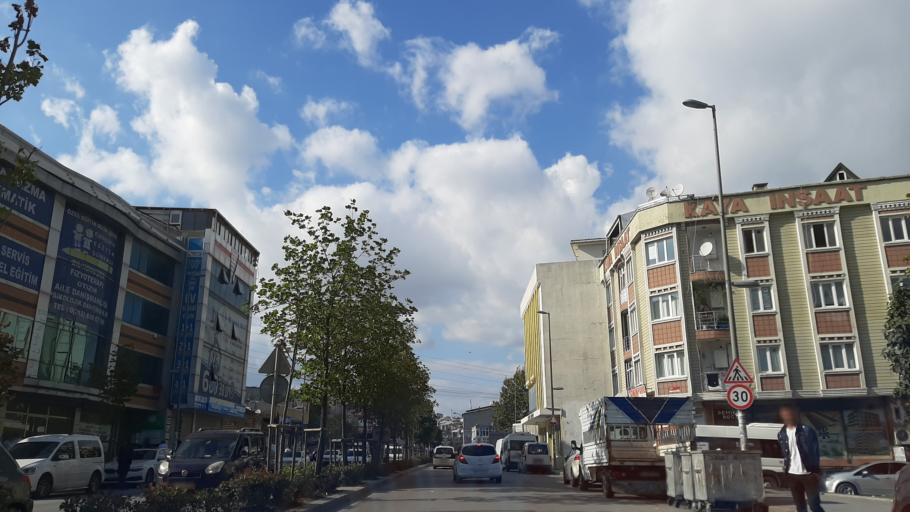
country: TR
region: Istanbul
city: Esenyurt
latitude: 41.0311
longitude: 28.6627
